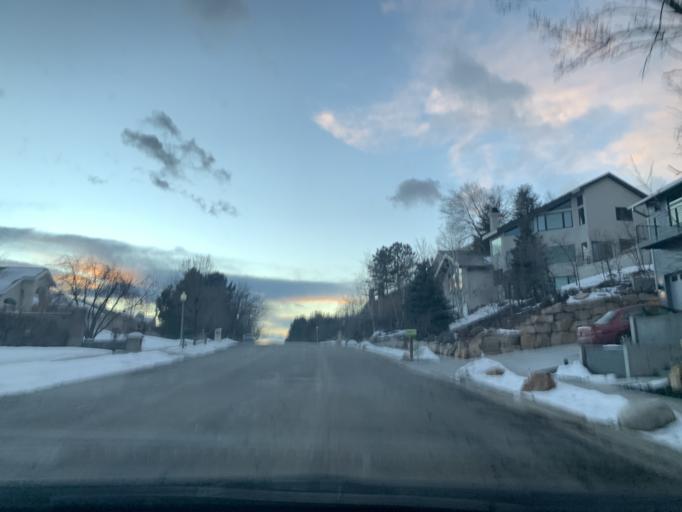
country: US
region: Utah
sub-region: Salt Lake County
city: Salt Lake City
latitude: 40.7831
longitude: -111.8456
